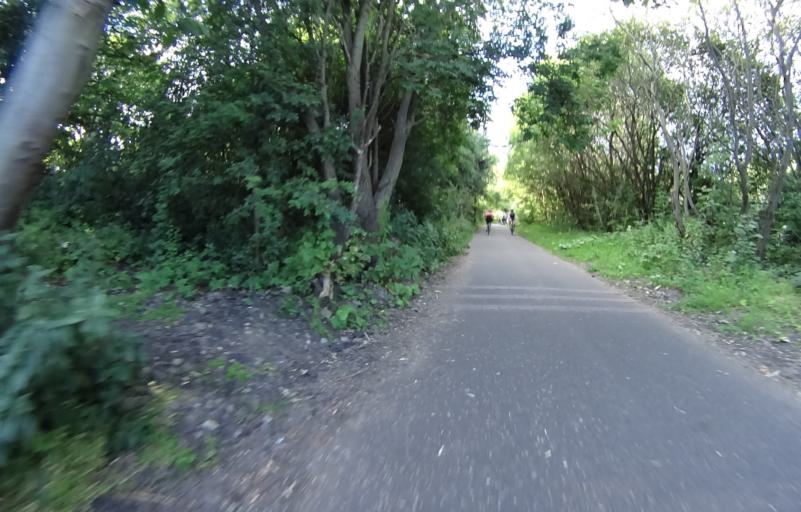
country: GB
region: Scotland
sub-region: Edinburgh
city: Edinburgh
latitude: 55.9586
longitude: -3.2449
